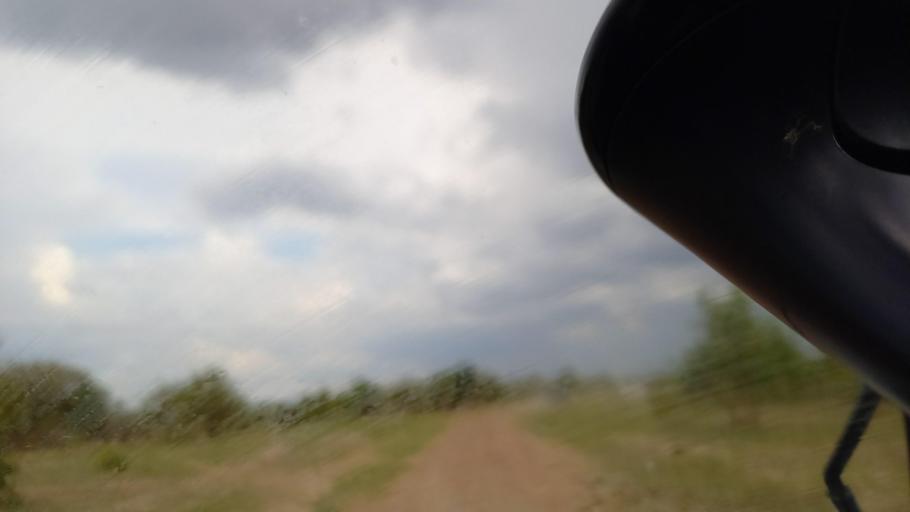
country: ZM
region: Lusaka
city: Kafue
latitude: -15.8540
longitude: 28.1175
